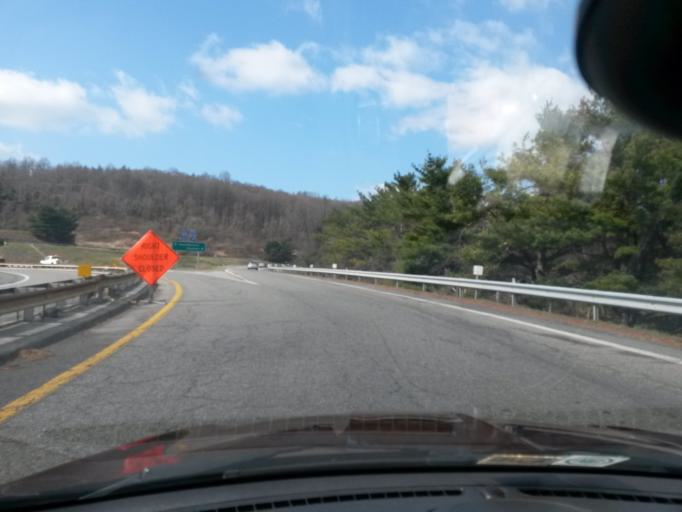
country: US
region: Virginia
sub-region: City of Waynesboro
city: Waynesboro
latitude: 38.0341
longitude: -78.8617
